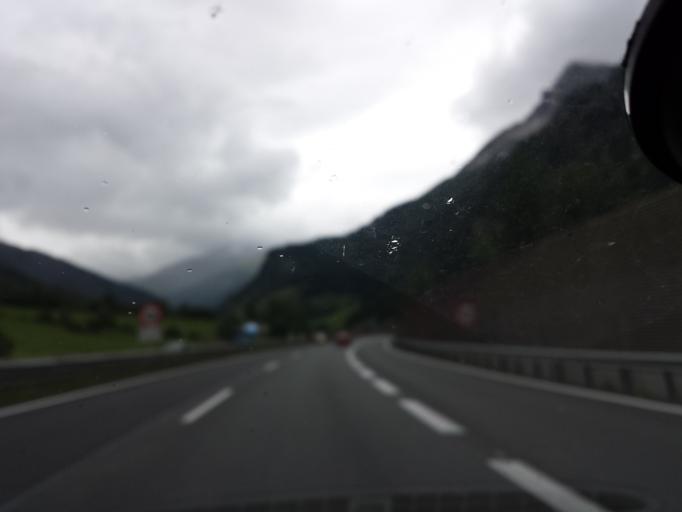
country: AT
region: Salzburg
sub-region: Politischer Bezirk Tamsweg
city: Zederhaus
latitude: 47.1600
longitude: 13.4836
